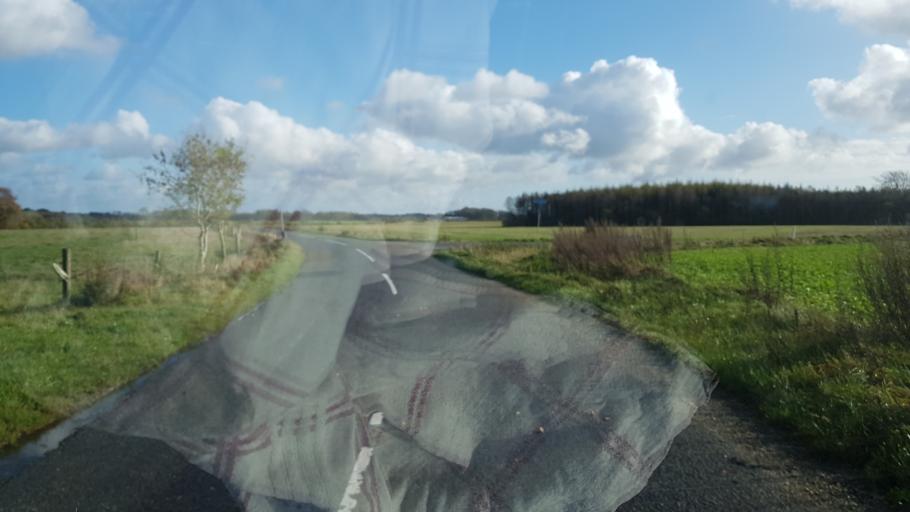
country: DK
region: South Denmark
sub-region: Varde Kommune
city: Olgod
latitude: 55.6906
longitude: 8.6863
